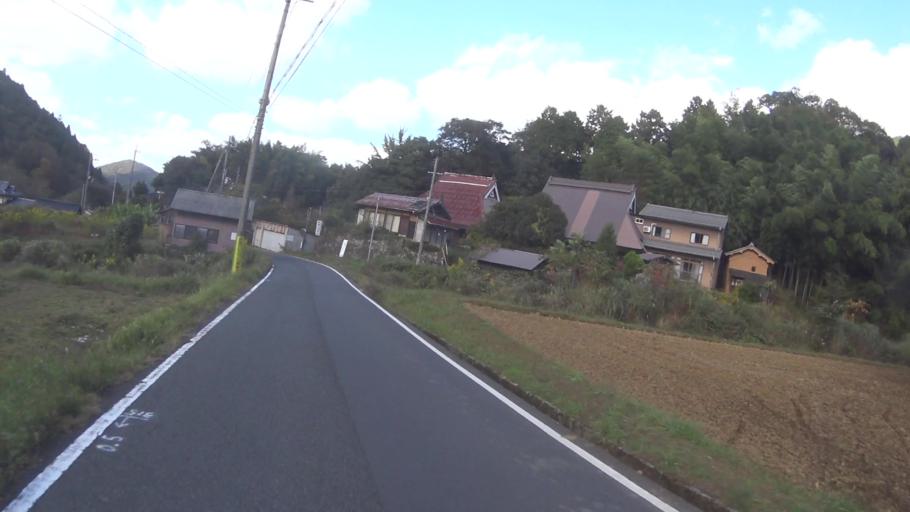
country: JP
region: Kyoto
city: Maizuru
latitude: 35.5427
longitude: 135.4521
